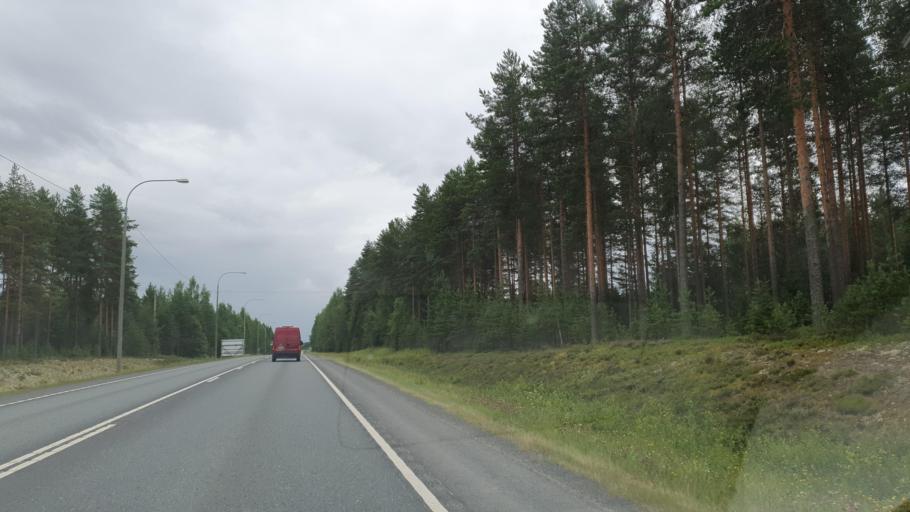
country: FI
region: Northern Savo
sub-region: Ylae-Savo
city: Lapinlahti
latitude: 63.2685
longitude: 27.4643
